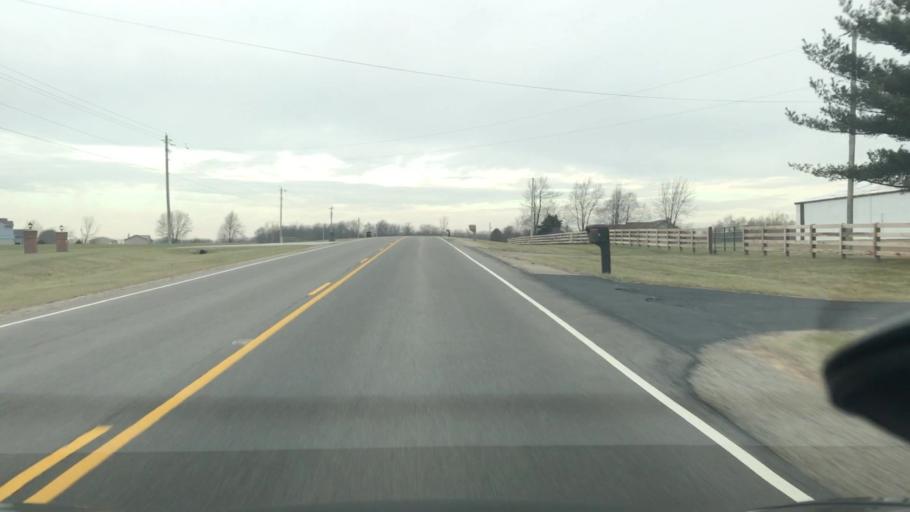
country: US
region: Ohio
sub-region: Madison County
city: London
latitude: 39.8451
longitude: -83.3906
